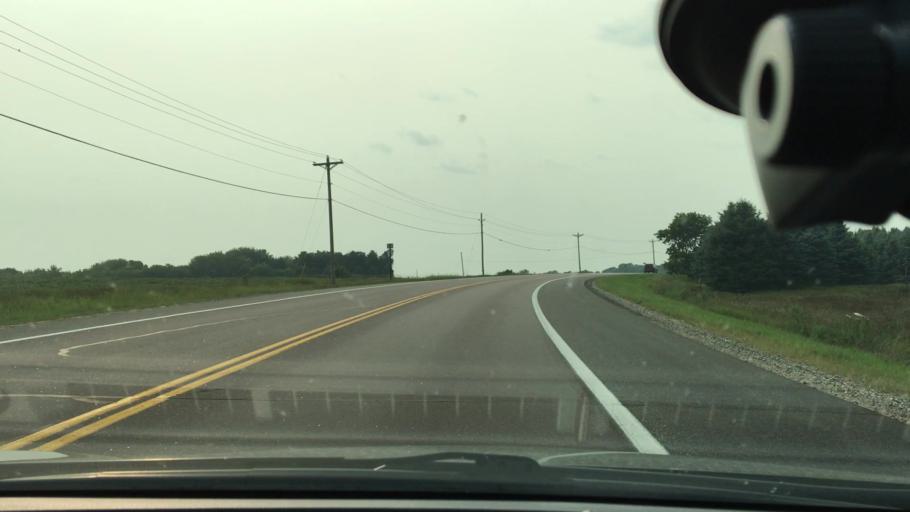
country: US
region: Minnesota
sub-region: Hennepin County
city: Dayton
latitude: 45.2447
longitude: -93.5282
